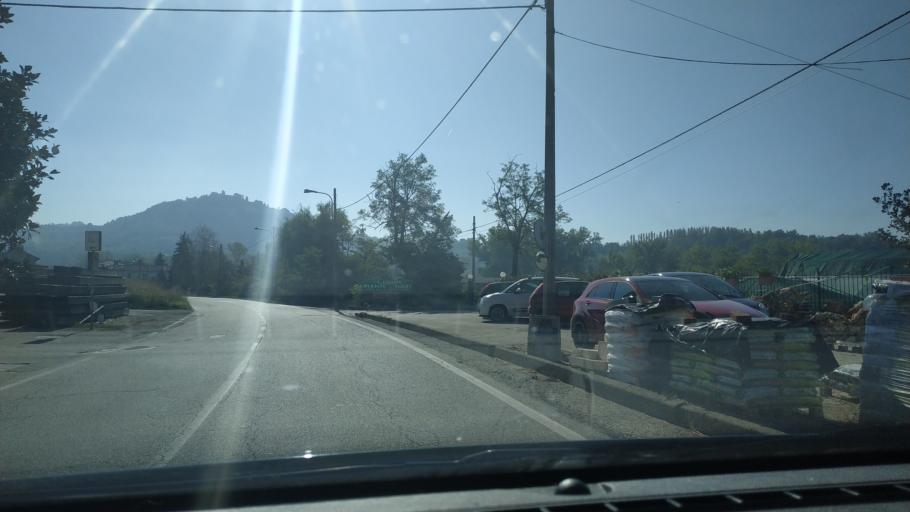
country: IT
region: Piedmont
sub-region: Provincia di Alessandria
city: Murisengo
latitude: 45.0826
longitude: 8.1528
